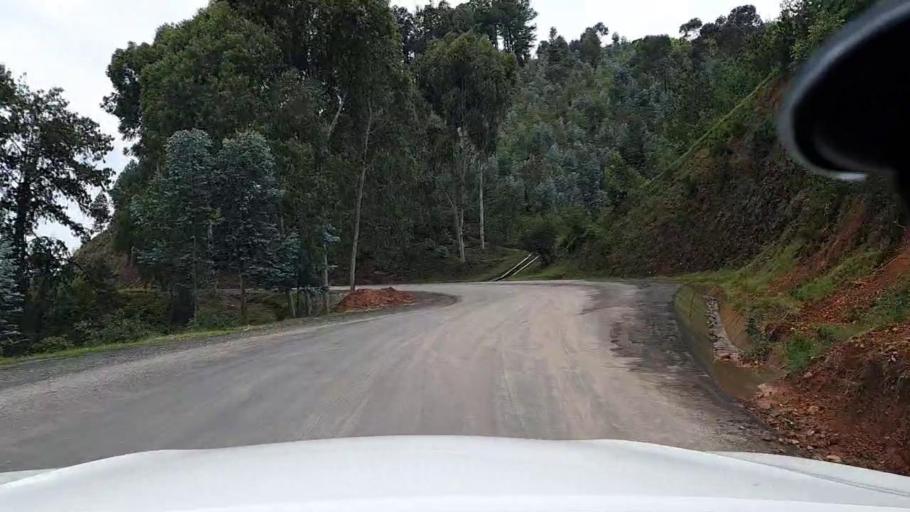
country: RW
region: Southern Province
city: Gitarama
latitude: -2.0643
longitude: 29.5590
